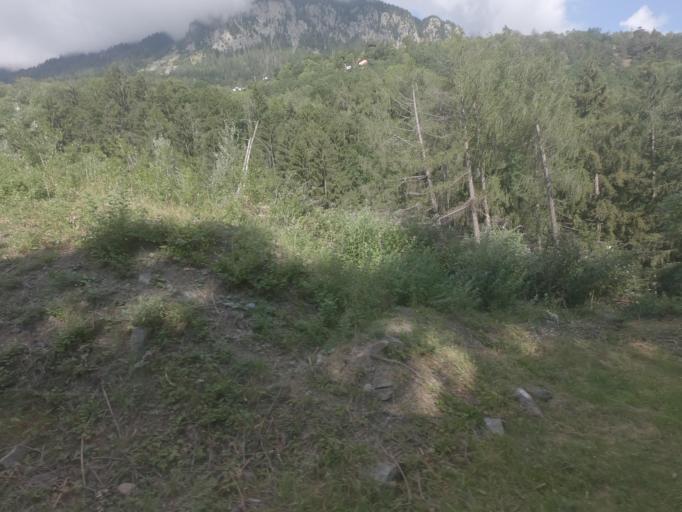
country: CH
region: Valais
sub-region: Saint-Maurice District
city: Vernayaz
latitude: 46.1270
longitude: 7.0280
